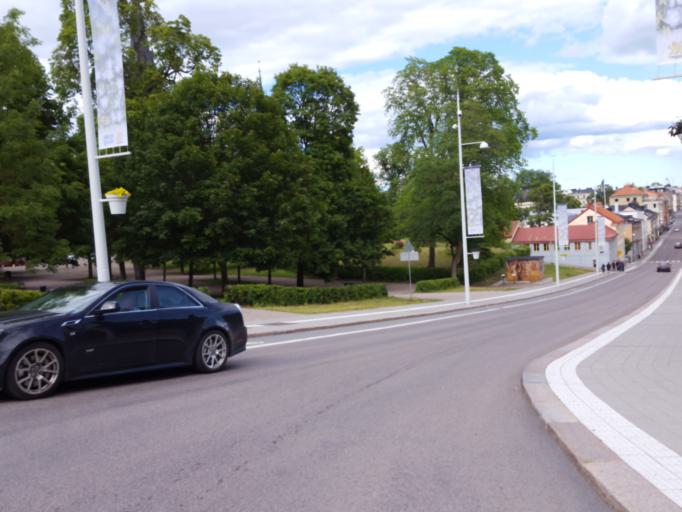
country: SE
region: Uppsala
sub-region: Uppsala Kommun
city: Uppsala
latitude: 59.8553
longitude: 17.6322
